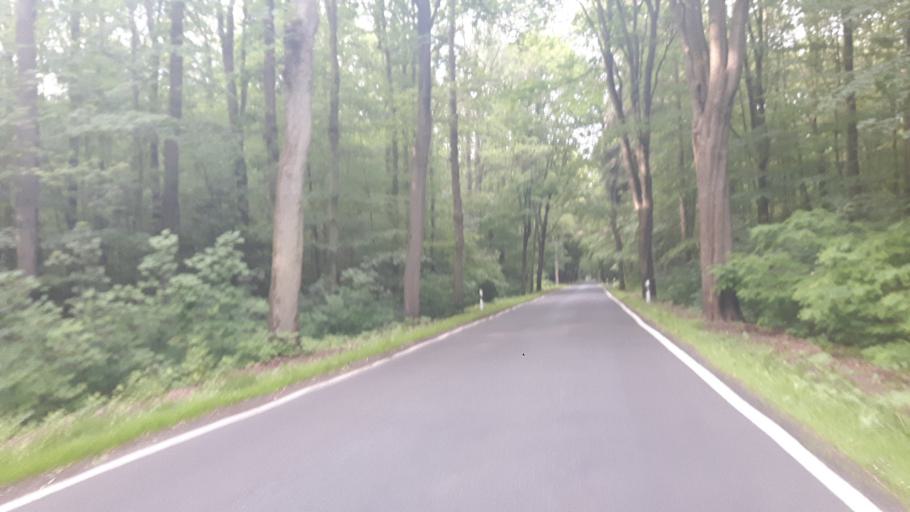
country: DE
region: Brandenburg
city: Hohenfinow
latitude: 52.7810
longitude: 13.8947
